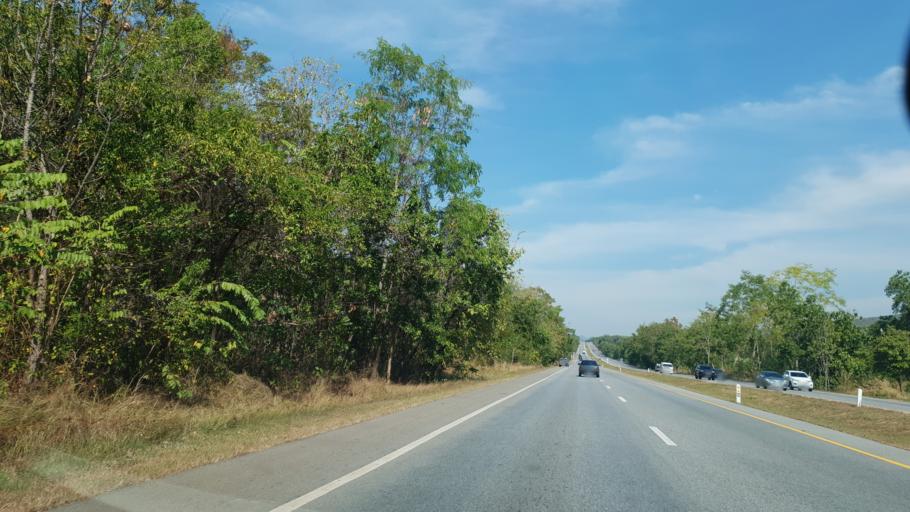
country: TH
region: Uttaradit
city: Thong Saen Khan
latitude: 17.4350
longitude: 100.2292
